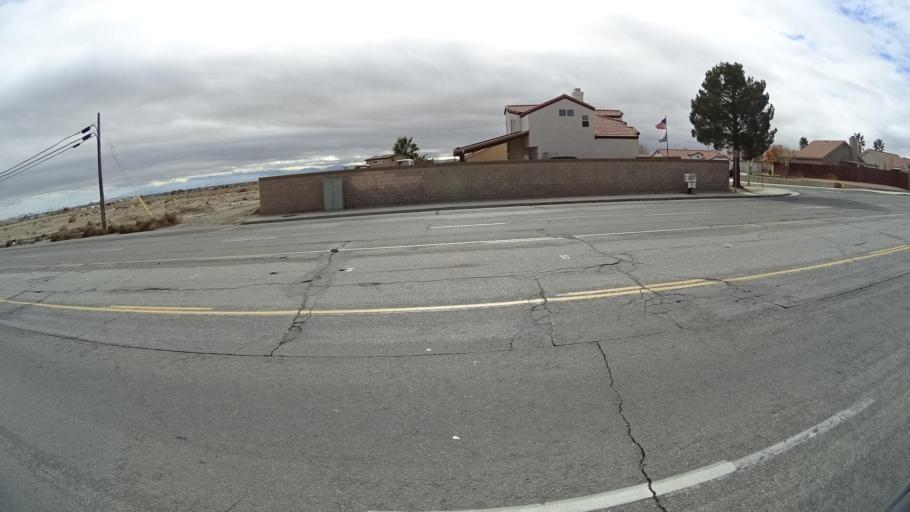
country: US
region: California
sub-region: Kern County
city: Rosamond
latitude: 34.8640
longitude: -118.1893
